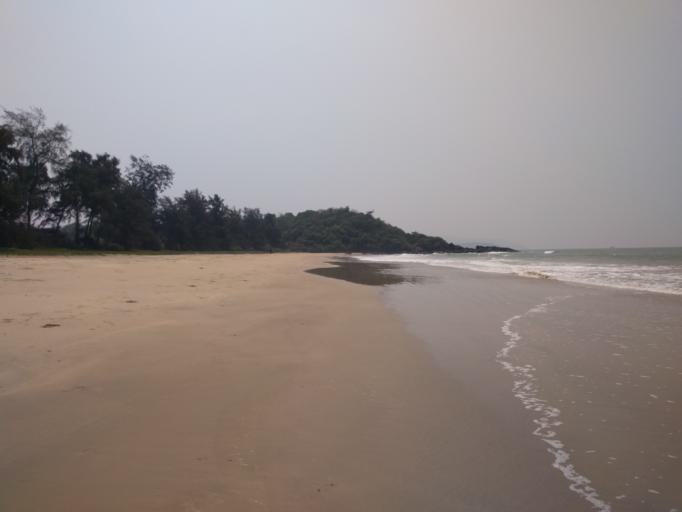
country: IN
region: Karnataka
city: Canacona
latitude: 14.9762
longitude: 74.0426
